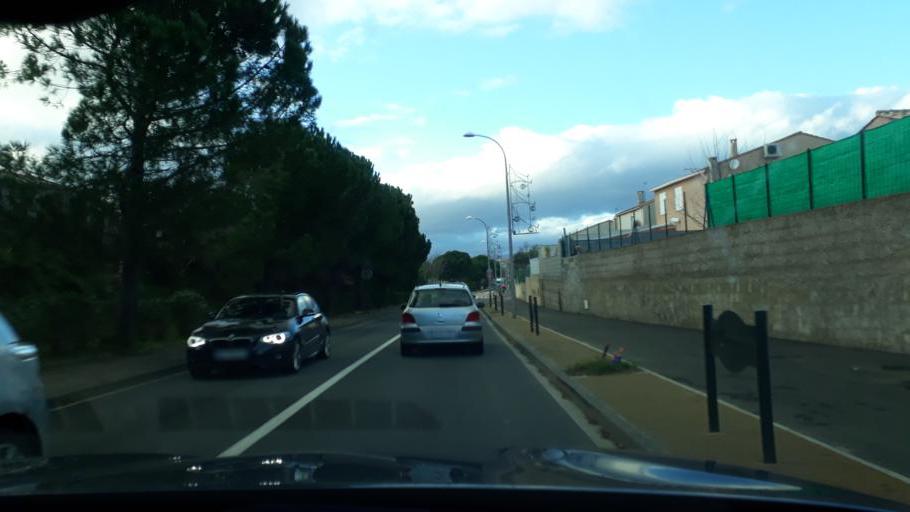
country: FR
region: Languedoc-Roussillon
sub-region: Departement de l'Herault
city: Colombiers
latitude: 43.3115
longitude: 3.1469
